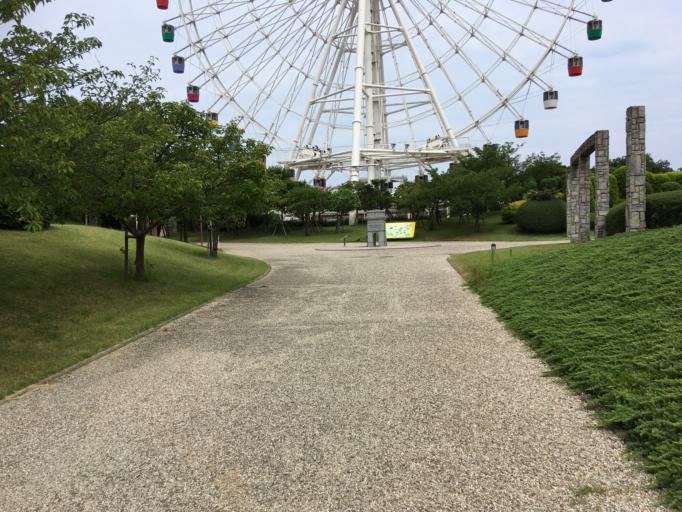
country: JP
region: Hyogo
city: Sumoto
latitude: 34.4157
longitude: 134.8987
